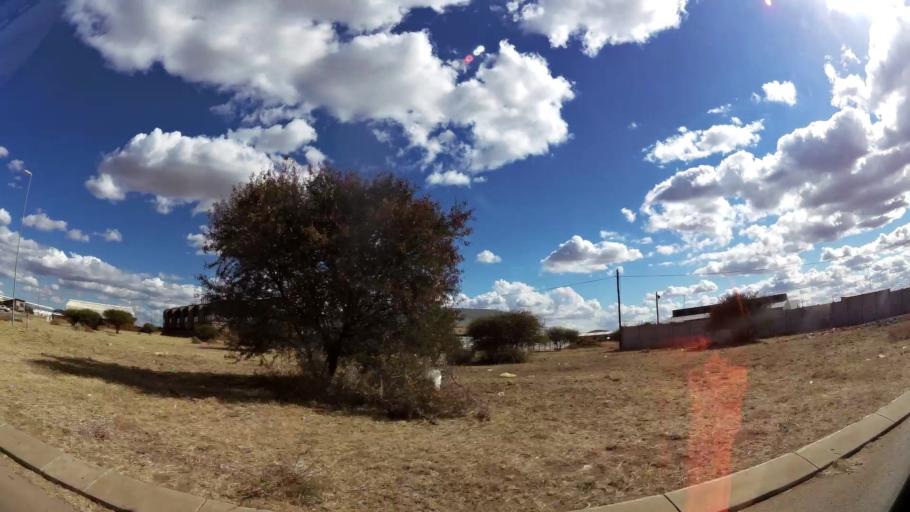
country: ZA
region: Limpopo
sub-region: Capricorn District Municipality
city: Polokwane
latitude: -23.8662
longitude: 29.4825
